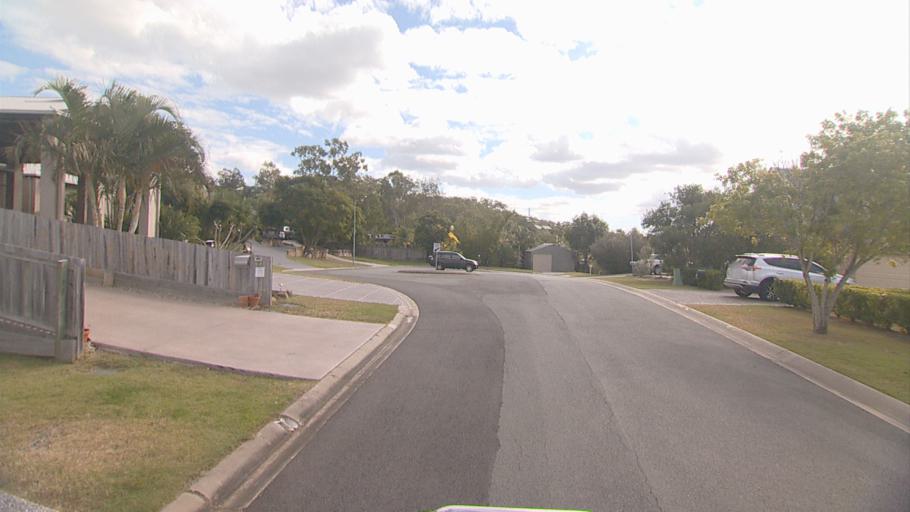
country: AU
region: Queensland
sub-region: Logan
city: Windaroo
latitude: -27.7343
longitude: 153.2056
